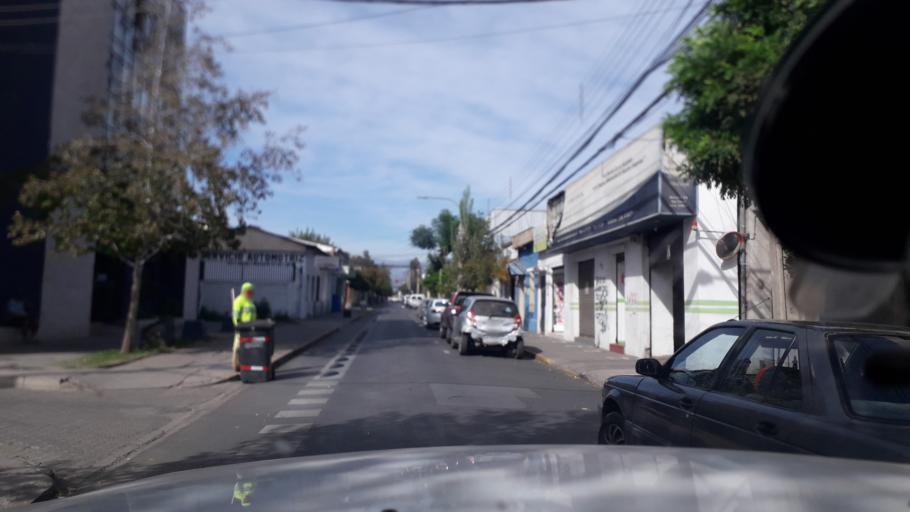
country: CL
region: Valparaiso
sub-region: Provincia de San Felipe
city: San Felipe
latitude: -32.7502
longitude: -70.7294
